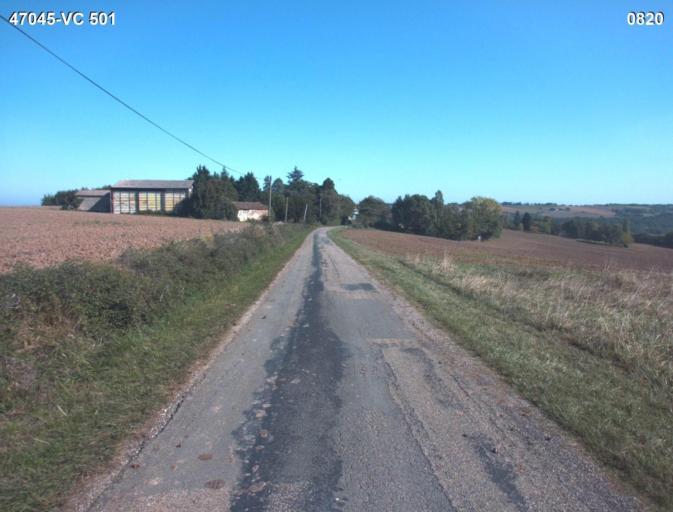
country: FR
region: Aquitaine
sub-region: Departement du Lot-et-Garonne
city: Nerac
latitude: 44.1580
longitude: 0.4077
